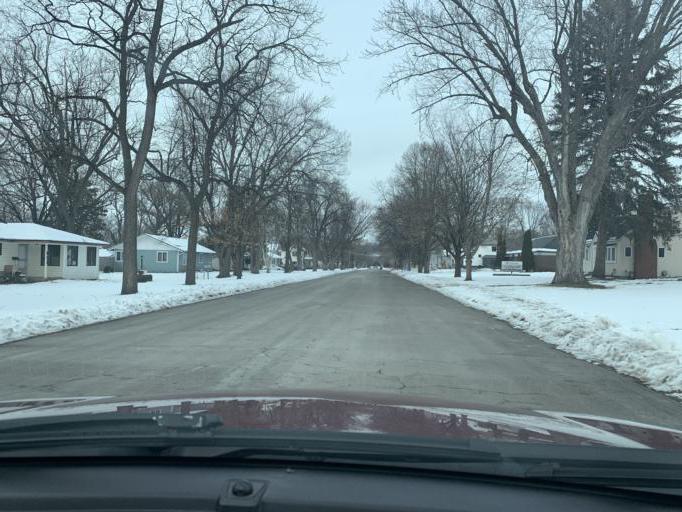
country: US
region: Minnesota
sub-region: Washington County
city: Saint Paul Park
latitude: 44.8424
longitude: -92.9900
